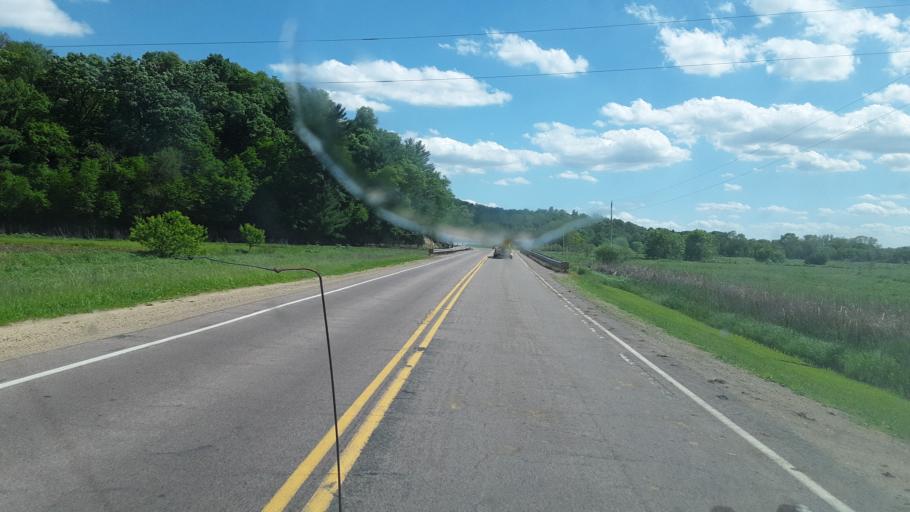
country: US
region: Wisconsin
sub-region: Richland County
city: Richland Center
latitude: 43.3671
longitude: -90.2658
